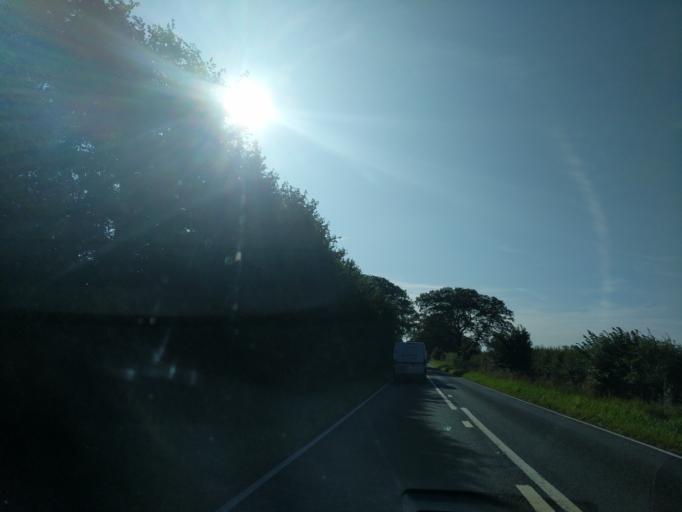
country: GB
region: England
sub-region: Lincolnshire
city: Bourne
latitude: 52.8032
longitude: -0.4776
